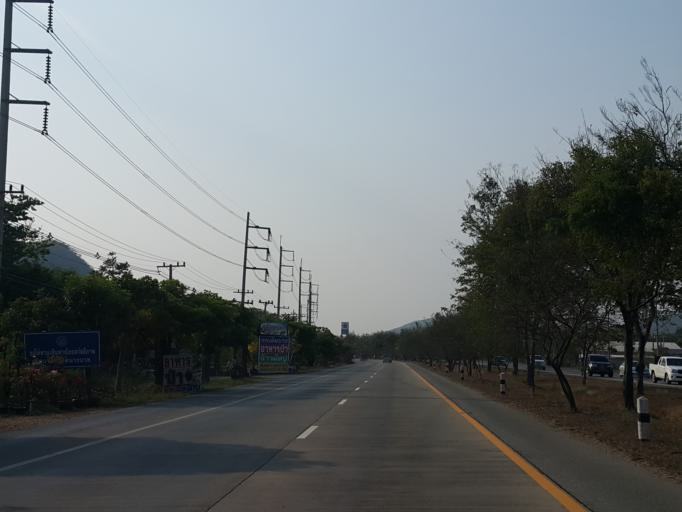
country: TH
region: Suphan Buri
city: Doembang Nangbuat
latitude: 14.8332
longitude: 100.1123
